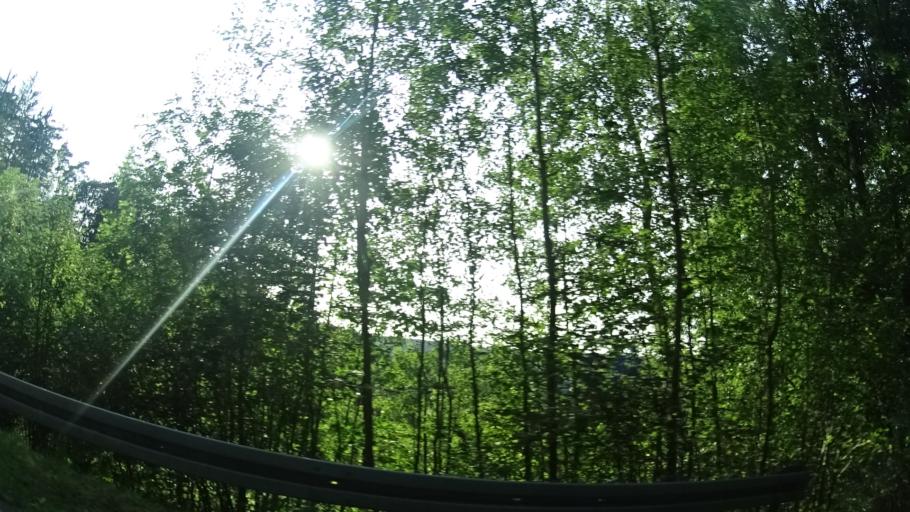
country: DE
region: Hesse
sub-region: Regierungsbezirk Darmstadt
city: Beerfelden
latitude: 49.5494
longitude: 8.9415
